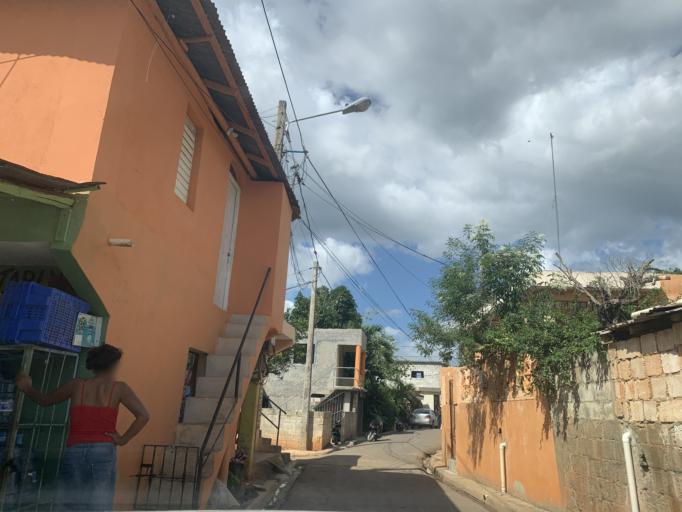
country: DO
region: Monte Plata
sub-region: Yamasa
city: Yamasa
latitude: 18.7719
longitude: -70.0284
